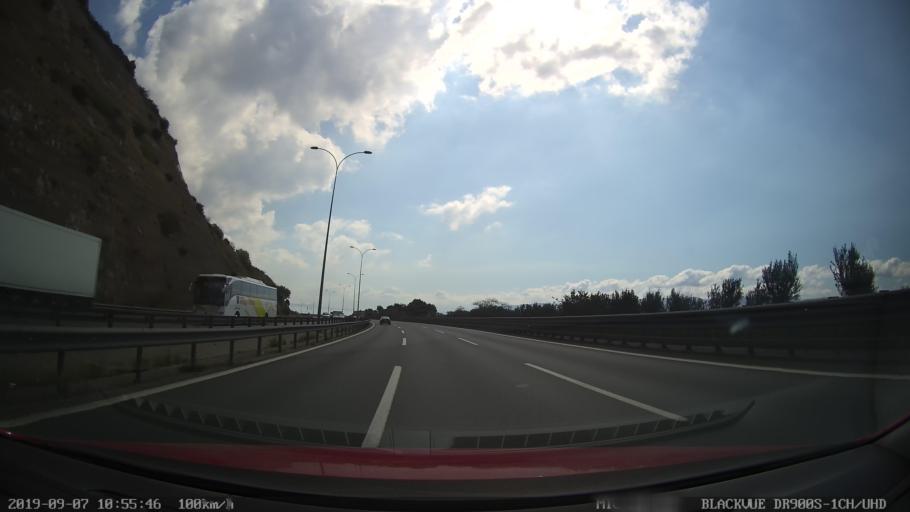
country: TR
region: Kocaeli
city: Hereke
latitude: 40.7772
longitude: 29.6327
